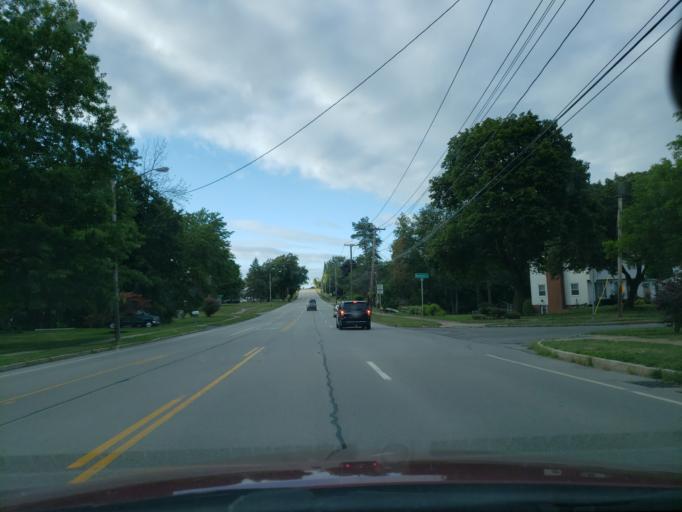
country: US
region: New York
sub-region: Monroe County
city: Greece
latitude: 43.2474
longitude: -77.6592
